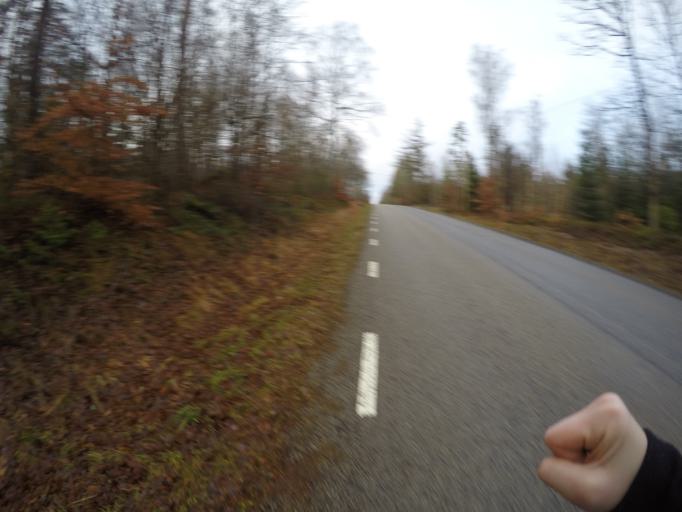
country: SE
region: Skane
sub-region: Osby Kommun
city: Lonsboda
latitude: 56.3786
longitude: 14.3445
